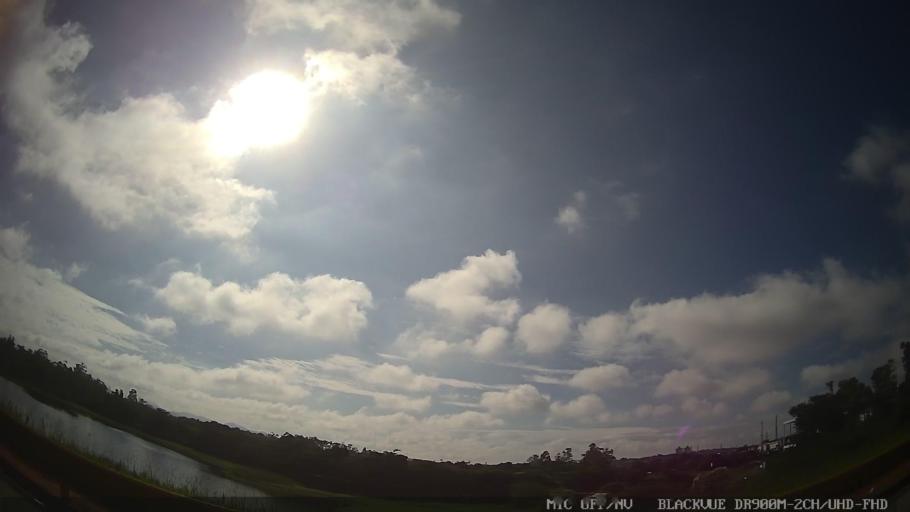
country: BR
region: Sao Paulo
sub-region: Itaquaquecetuba
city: Itaquaquecetuba
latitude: -23.4788
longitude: -46.3516
